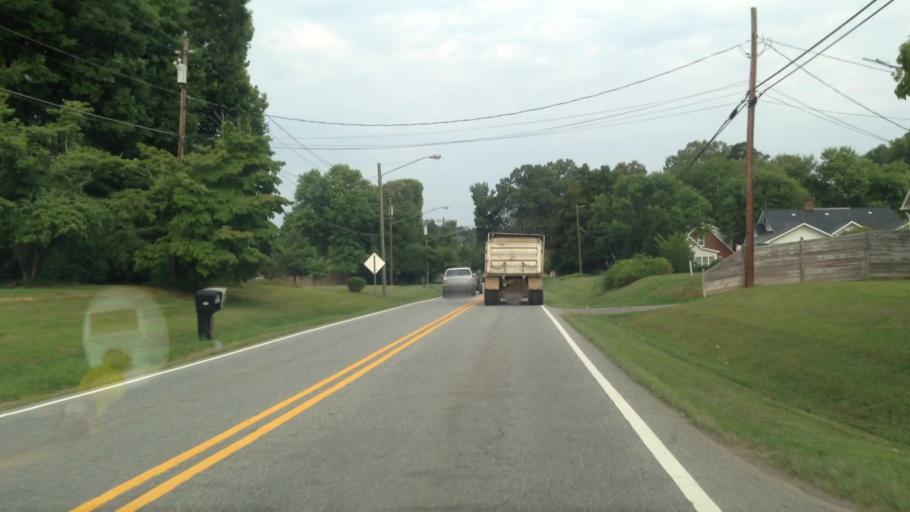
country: US
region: North Carolina
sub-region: Forsyth County
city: Rural Hall
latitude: 36.1914
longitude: -80.2332
